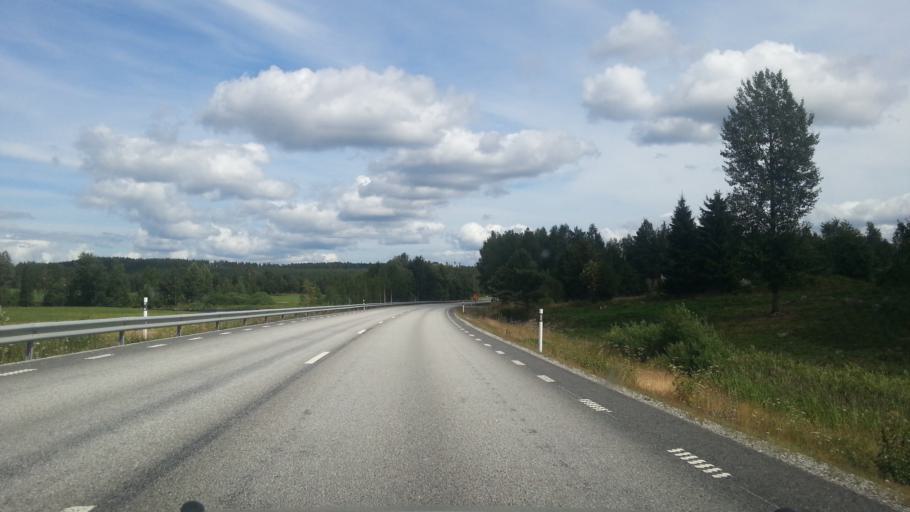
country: SE
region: OErebro
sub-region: Lindesbergs Kommun
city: Lindesberg
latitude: 59.7490
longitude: 15.4350
